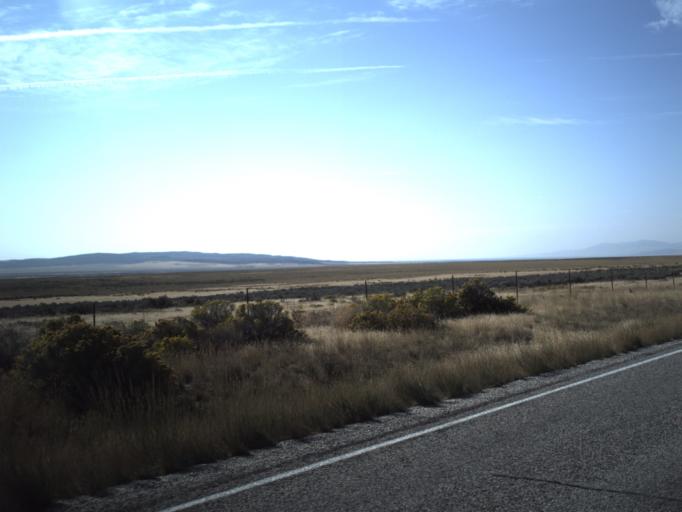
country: US
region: Idaho
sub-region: Oneida County
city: Malad City
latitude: 41.9308
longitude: -113.0896
